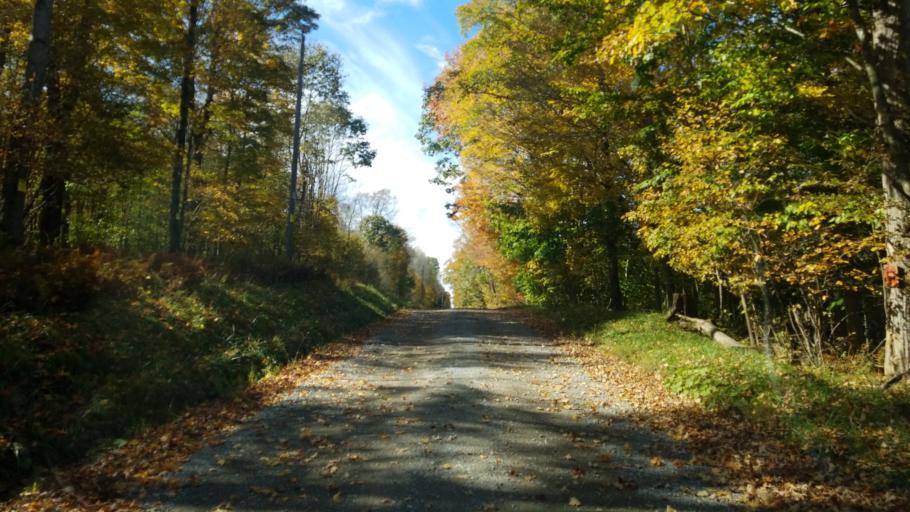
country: US
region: Pennsylvania
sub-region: Jefferson County
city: Falls Creek
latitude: 41.1917
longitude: -78.7848
